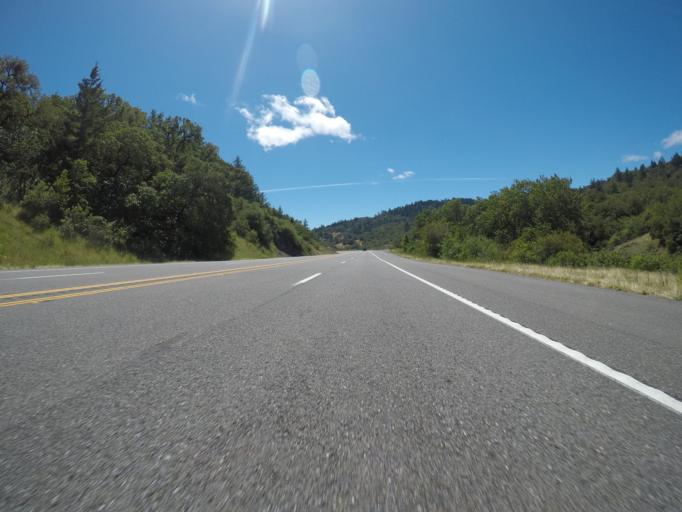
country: US
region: California
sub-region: Humboldt County
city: Redway
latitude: 40.1622
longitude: -123.7883
